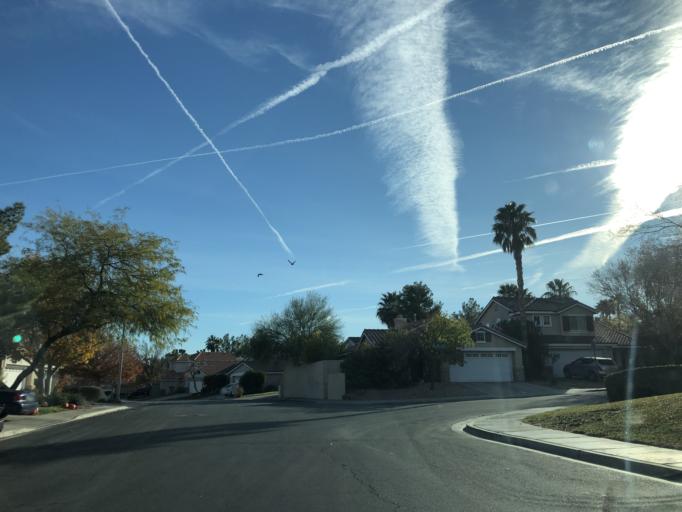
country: US
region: Nevada
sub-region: Clark County
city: Whitney
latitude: 36.0236
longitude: -115.0713
